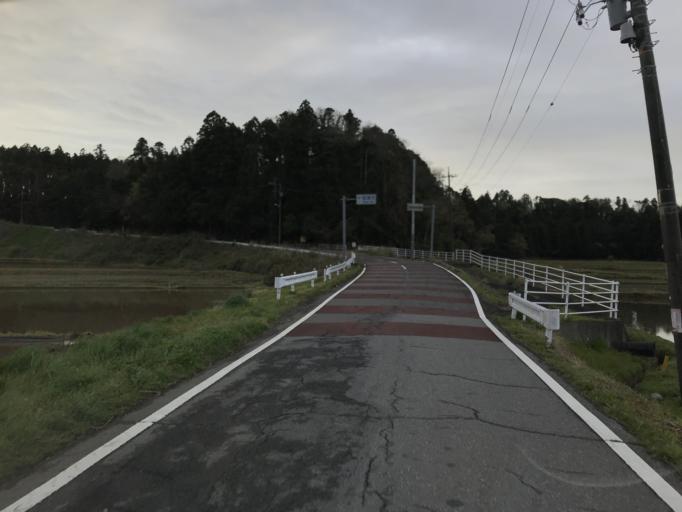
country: JP
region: Chiba
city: Yokaichiba
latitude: 35.7448
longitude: 140.5037
